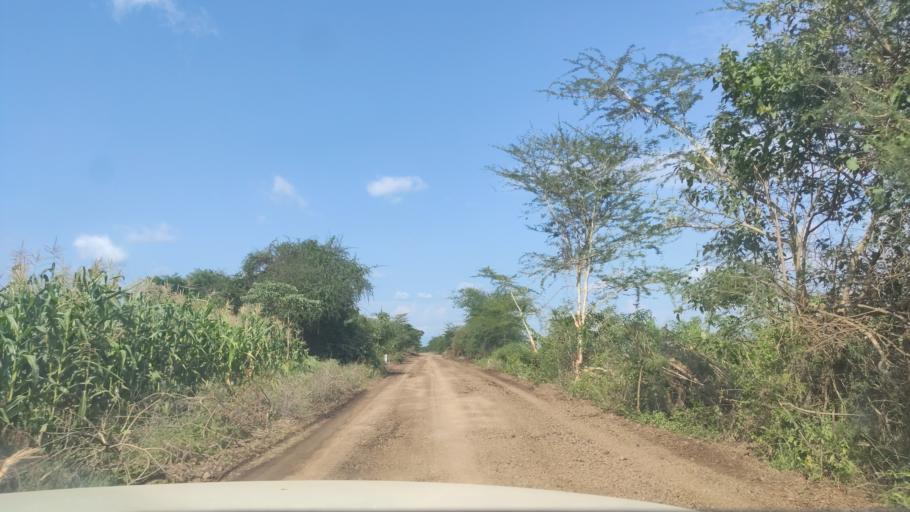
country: ET
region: Southern Nations, Nationalities, and People's Region
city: Felege Neway
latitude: 6.3793
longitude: 37.0901
